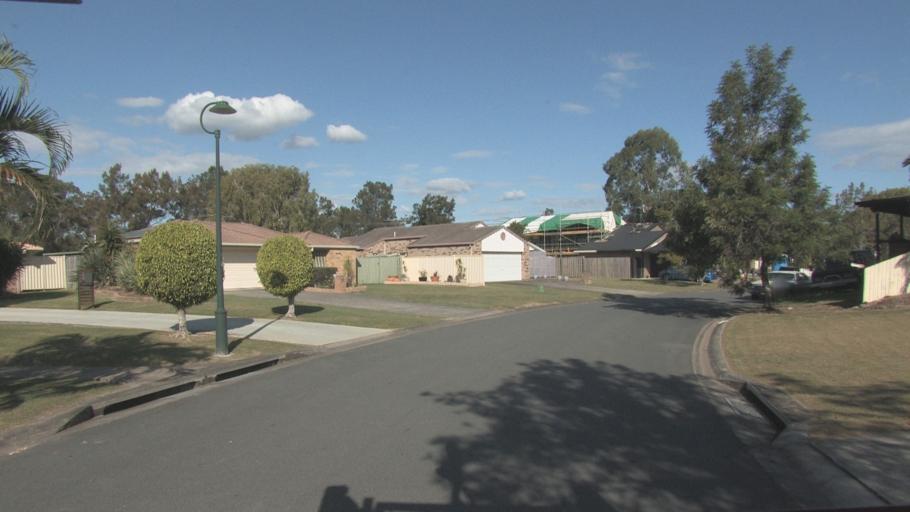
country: AU
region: Queensland
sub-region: Logan
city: Windaroo
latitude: -27.7515
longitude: 153.1955
